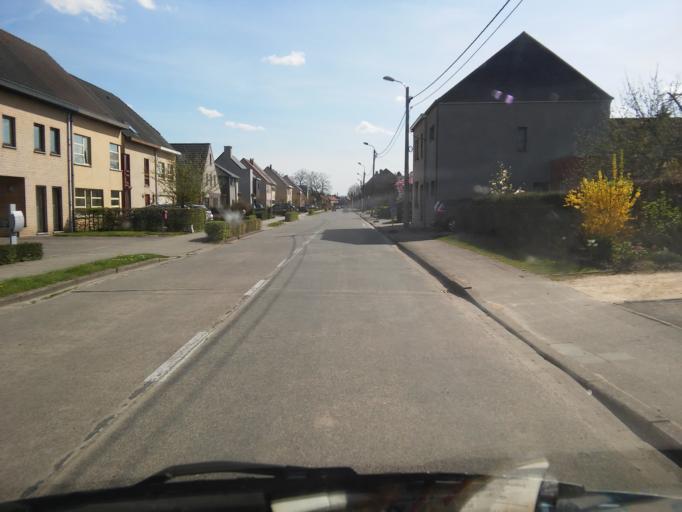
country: BE
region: Flanders
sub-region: Provincie Antwerpen
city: Willebroek
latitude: 51.0534
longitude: 4.3812
